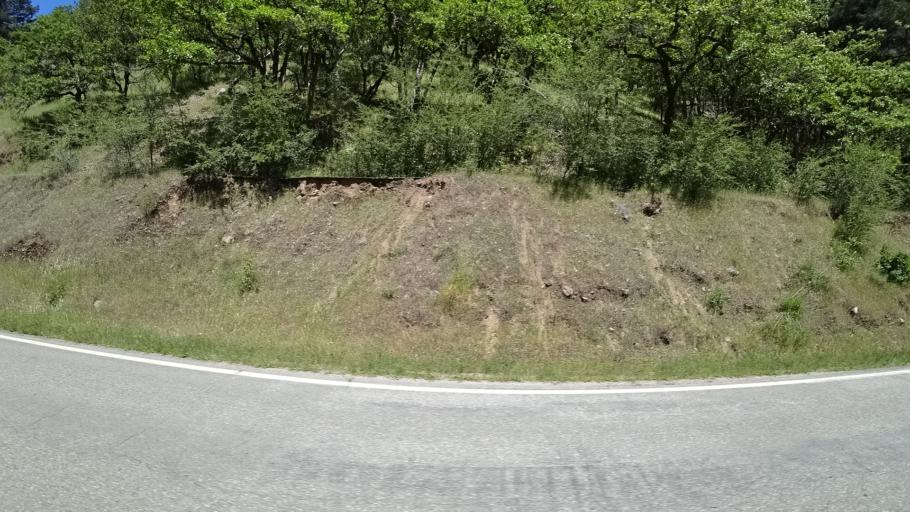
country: US
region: California
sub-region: Trinity County
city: Hayfork
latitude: 40.7525
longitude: -123.2821
